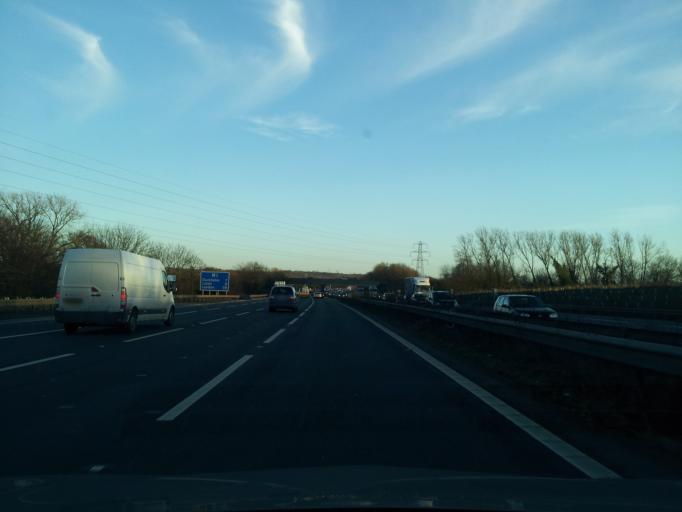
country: GB
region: England
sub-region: Central Bedfordshire
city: Toddington
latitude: 51.9558
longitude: -0.5135
